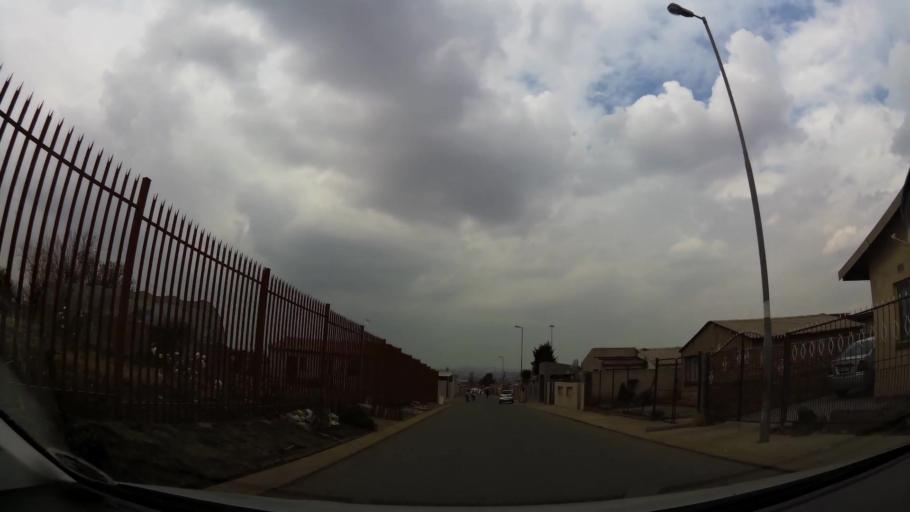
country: ZA
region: Gauteng
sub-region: City of Johannesburg Metropolitan Municipality
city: Soweto
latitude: -26.2613
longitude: 27.8620
